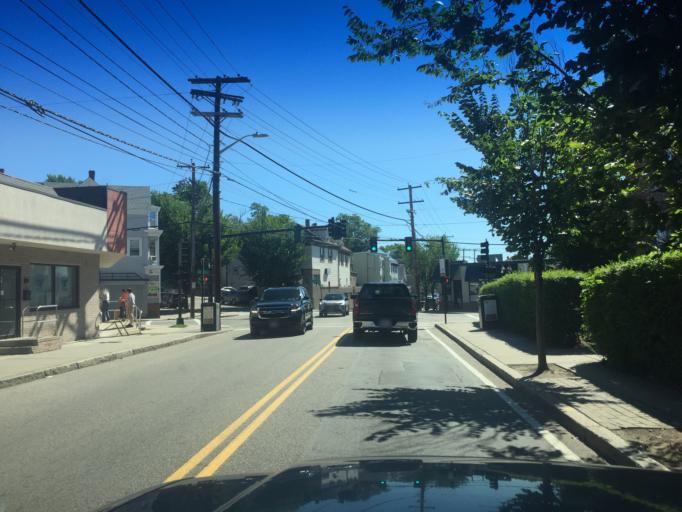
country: US
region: Massachusetts
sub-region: Norfolk County
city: Quincy
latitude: 42.2425
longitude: -71.0158
